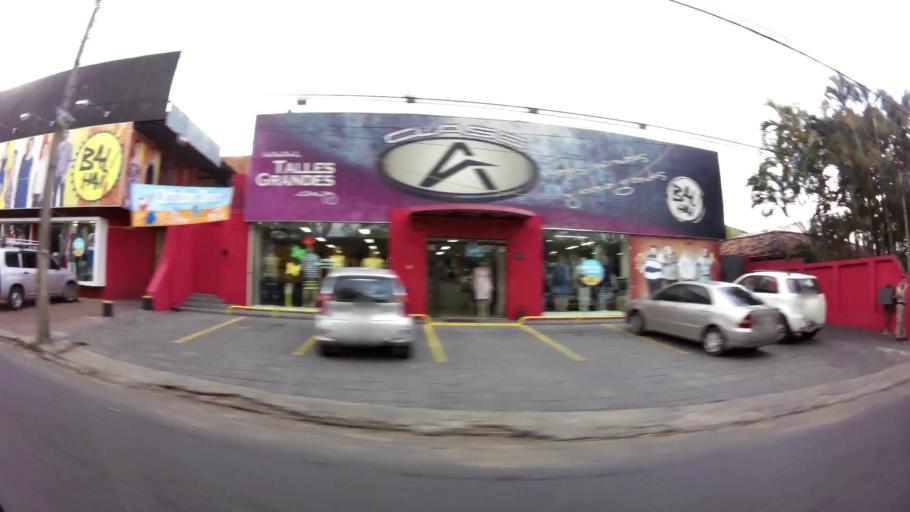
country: PY
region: Asuncion
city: Asuncion
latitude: -25.2891
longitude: -57.5896
